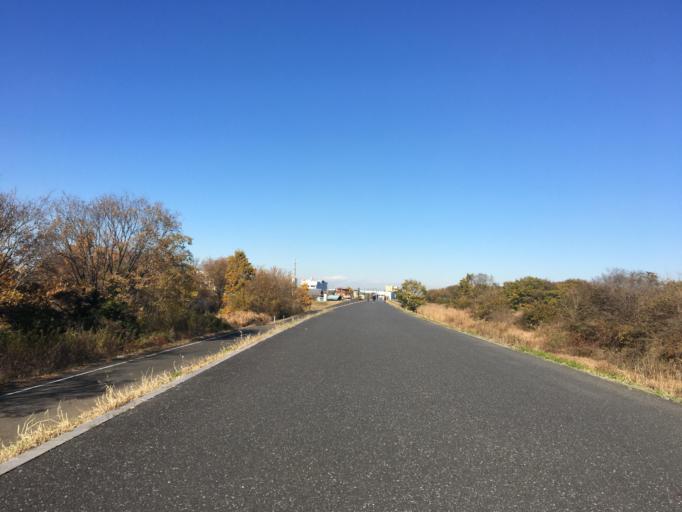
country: JP
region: Saitama
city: Yashio-shi
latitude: 35.8346
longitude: 139.8427
